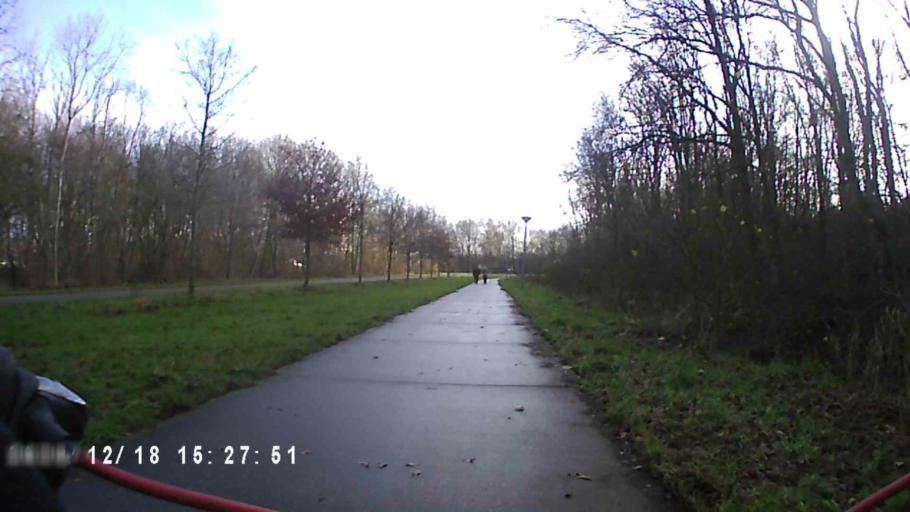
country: NL
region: Groningen
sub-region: Gemeente Hoogezand-Sappemeer
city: Hoogezand
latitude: 53.1480
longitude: 6.7061
